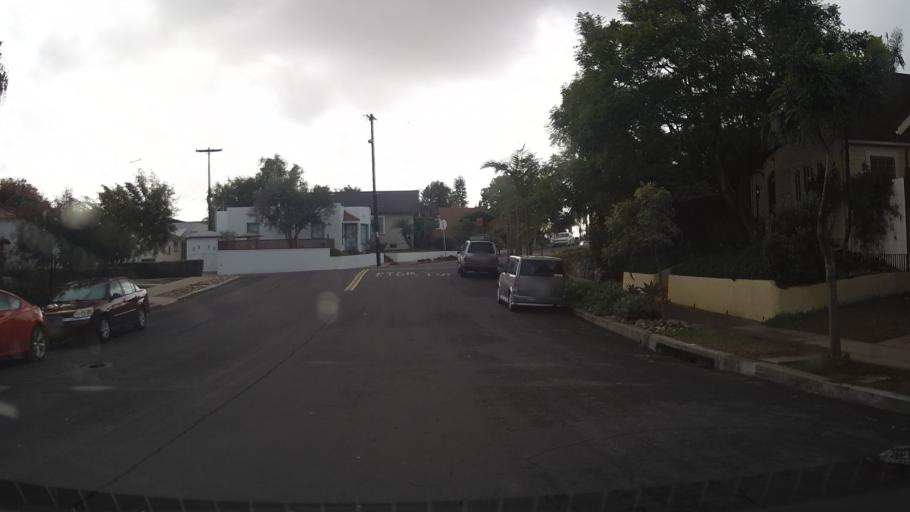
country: US
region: California
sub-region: San Diego County
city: San Diego
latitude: 32.7414
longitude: -117.1219
